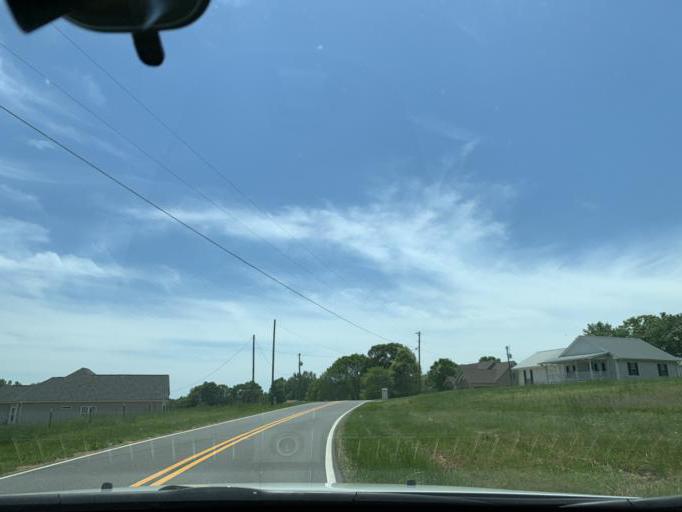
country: US
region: Georgia
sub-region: Hall County
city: Flowery Branch
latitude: 34.2784
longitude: -84.0231
